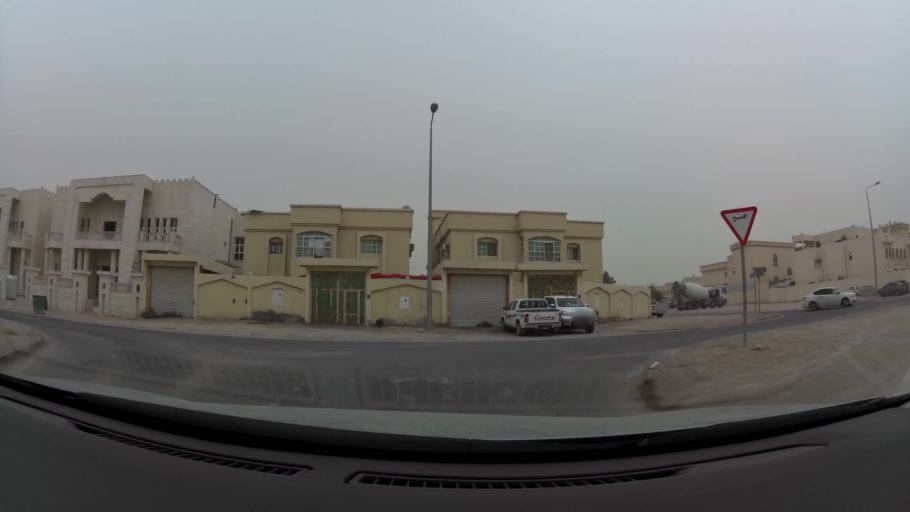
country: QA
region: Baladiyat ad Dawhah
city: Doha
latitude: 25.2396
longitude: 51.4891
